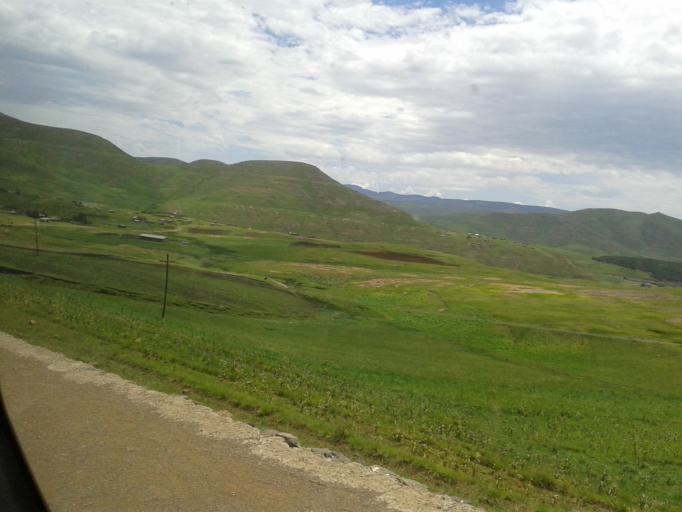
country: LS
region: Maseru
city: Nako
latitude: -29.8458
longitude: 28.0262
